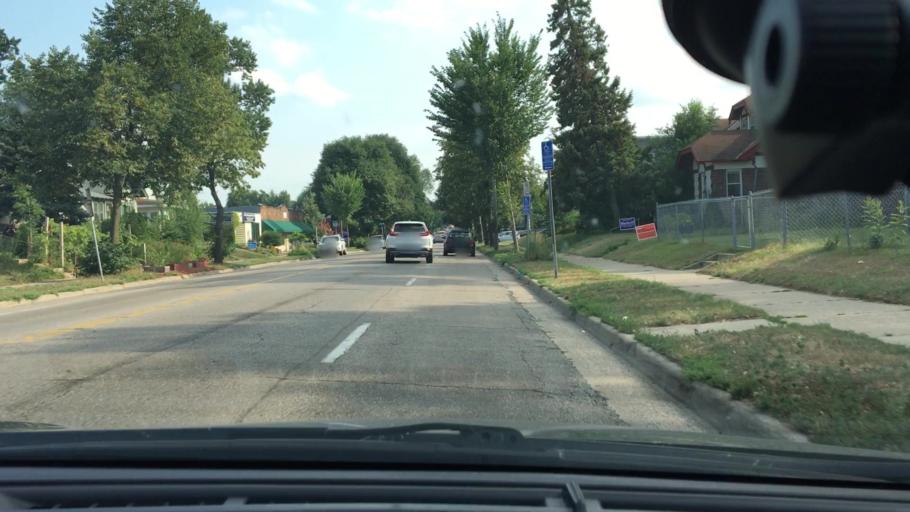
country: US
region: Minnesota
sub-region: Hennepin County
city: Minneapolis
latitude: 44.9370
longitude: -93.2475
